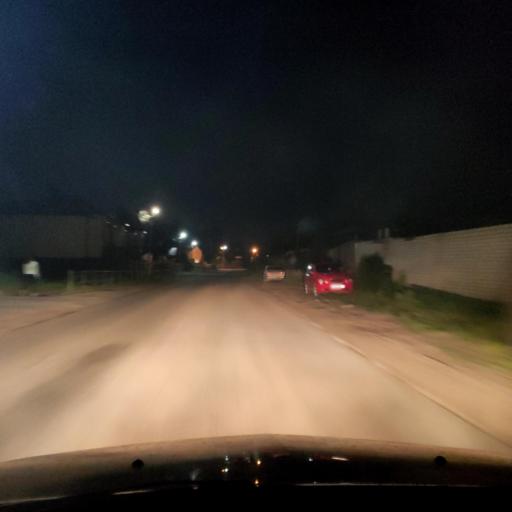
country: RU
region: Voronezj
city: Podgornoye
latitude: 51.7941
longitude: 39.1474
